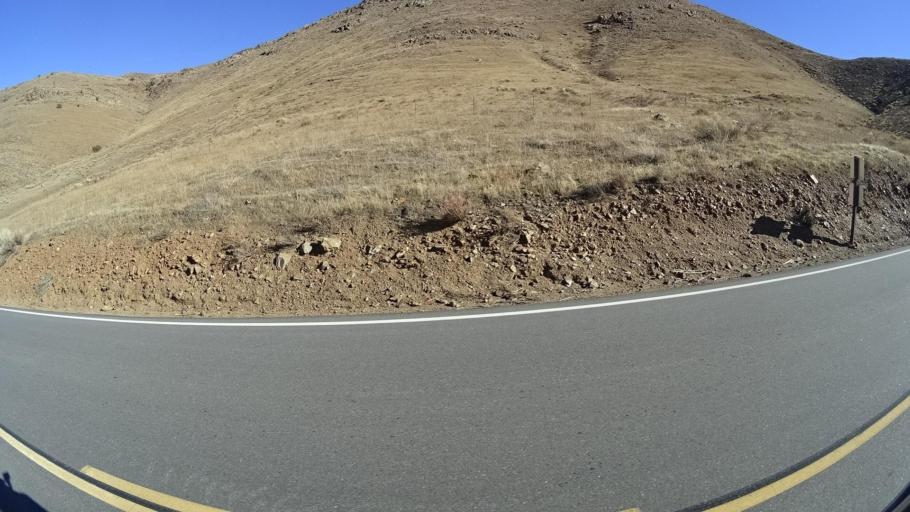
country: US
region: California
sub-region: Kern County
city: Wofford Heights
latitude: 35.6892
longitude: -118.4259
